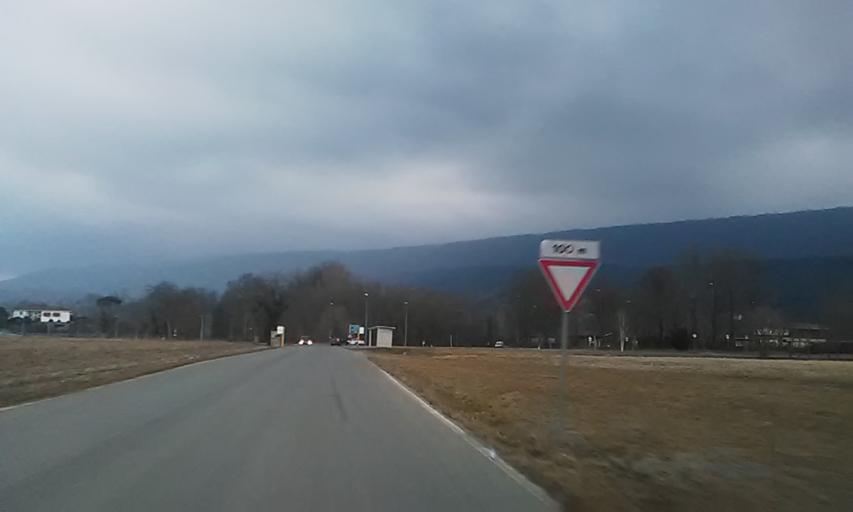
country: IT
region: Piedmont
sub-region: Provincia di Torino
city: Burolo
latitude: 45.4779
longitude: 7.9203
